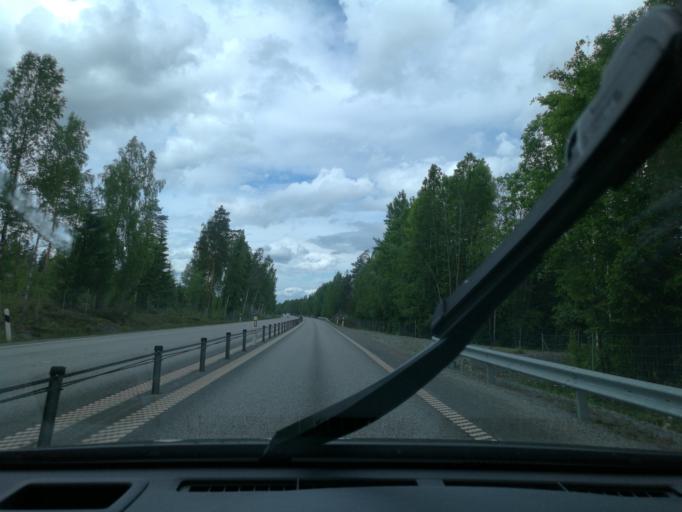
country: SE
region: Vaestmanland
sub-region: Surahammars Kommun
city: Surahammar
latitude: 59.7102
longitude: 16.2453
